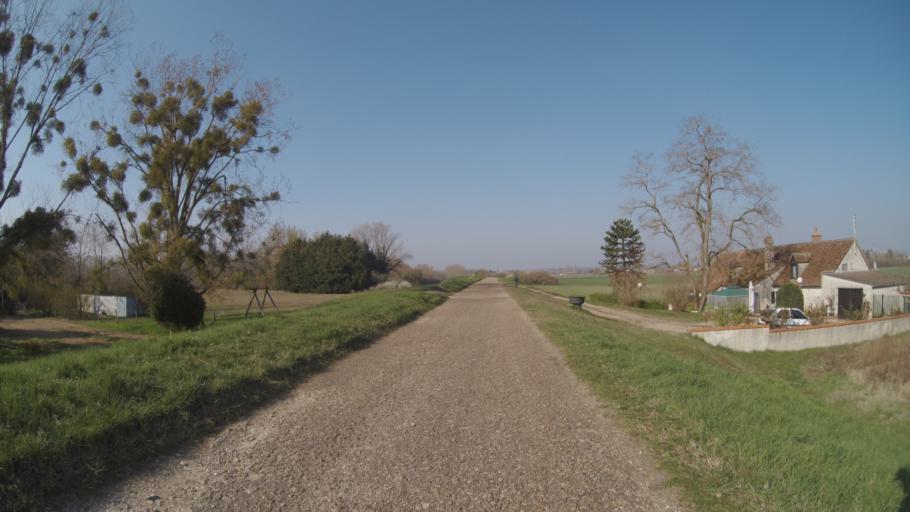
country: FR
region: Centre
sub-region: Departement du Loiret
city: Sandillon
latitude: 47.8684
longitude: 2.0369
